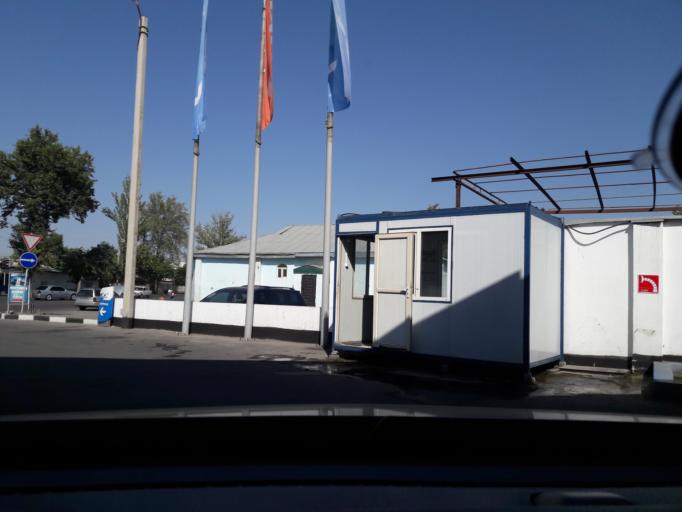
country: TJ
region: Dushanbe
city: Dushanbe
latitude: 38.5459
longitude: 68.7479
